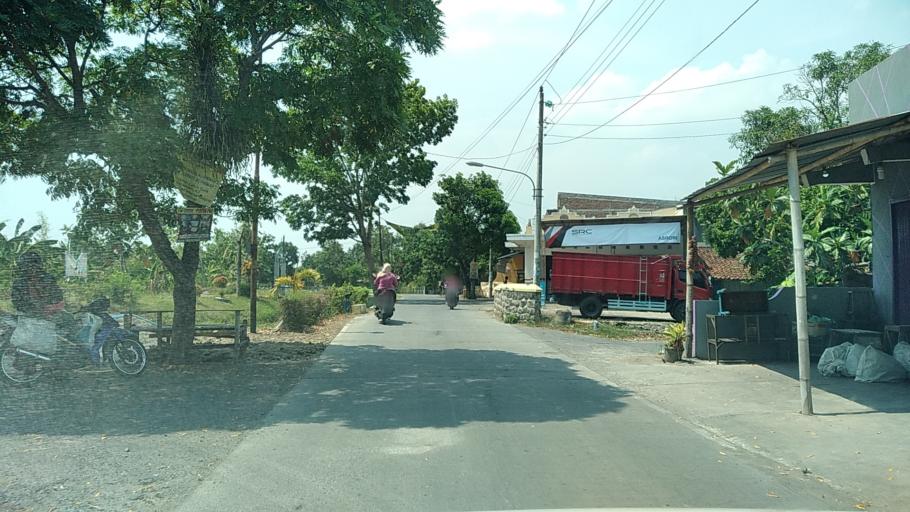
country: ID
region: Central Java
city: Mranggen
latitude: -7.0237
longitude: 110.4794
